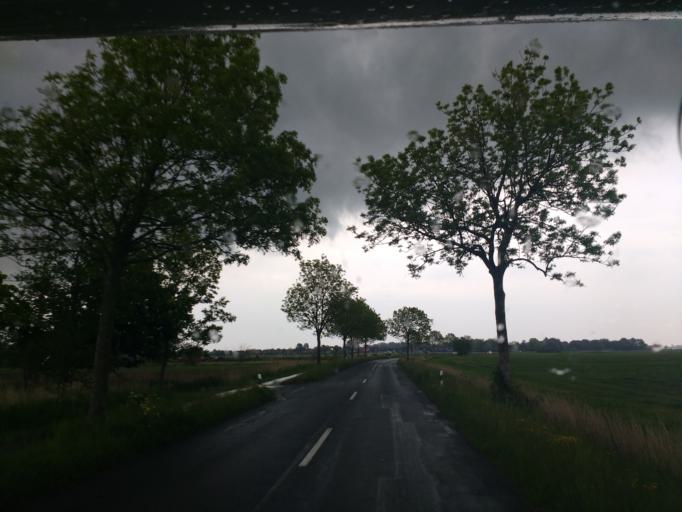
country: DE
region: Lower Saxony
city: Schillig
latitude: 53.7066
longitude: 7.9548
